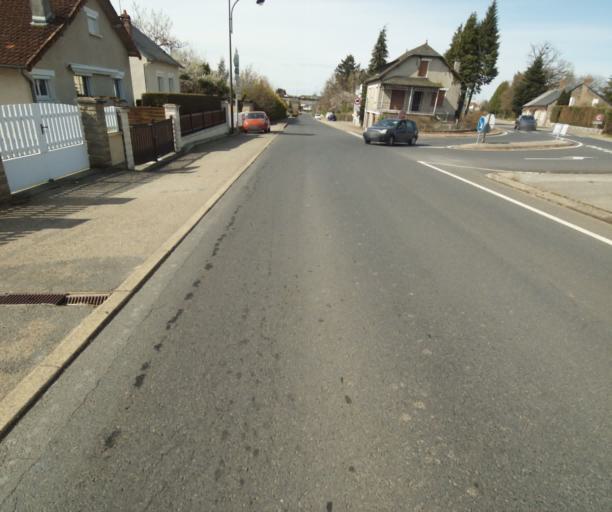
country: FR
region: Limousin
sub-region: Departement de la Correze
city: Seilhac
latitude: 45.3623
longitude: 1.7252
